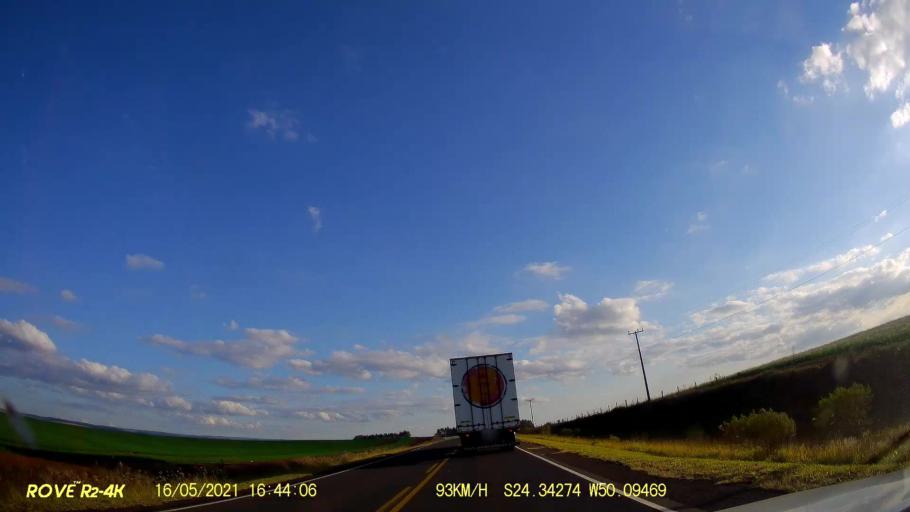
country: BR
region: Parana
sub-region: Pirai Do Sul
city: Pirai do Sul
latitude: -24.3428
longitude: -50.0948
